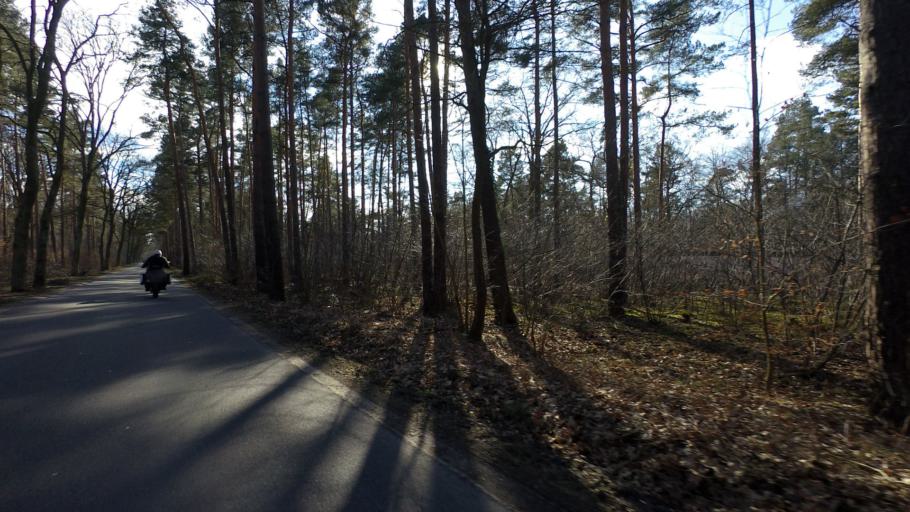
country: DE
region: Brandenburg
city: Oranienburg
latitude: 52.7596
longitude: 13.2815
